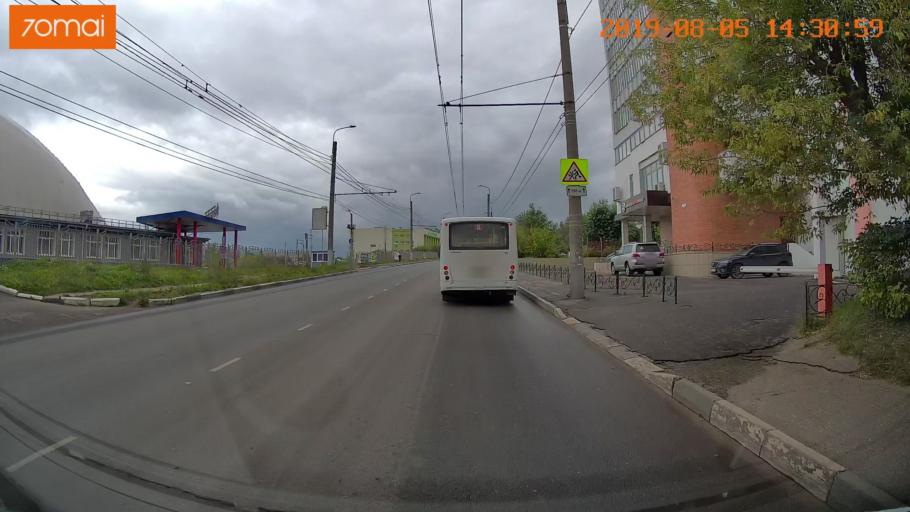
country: RU
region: Ivanovo
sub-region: Gorod Ivanovo
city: Ivanovo
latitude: 56.9853
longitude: 41.0069
